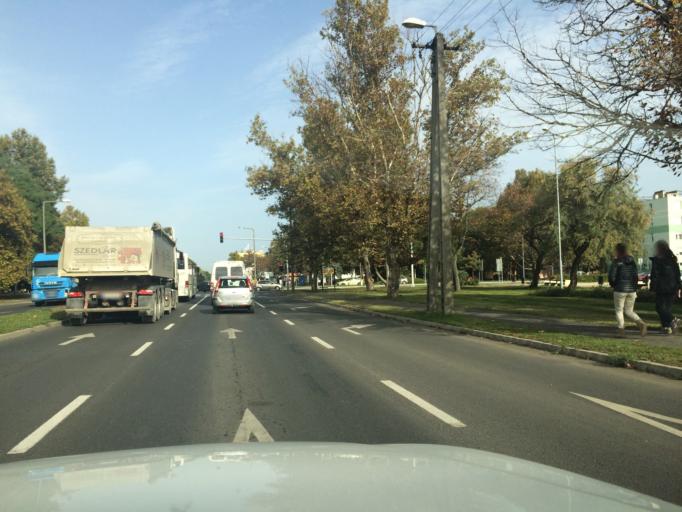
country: HU
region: Szabolcs-Szatmar-Bereg
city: Nyiregyhaza
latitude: 47.9459
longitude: 21.7070
